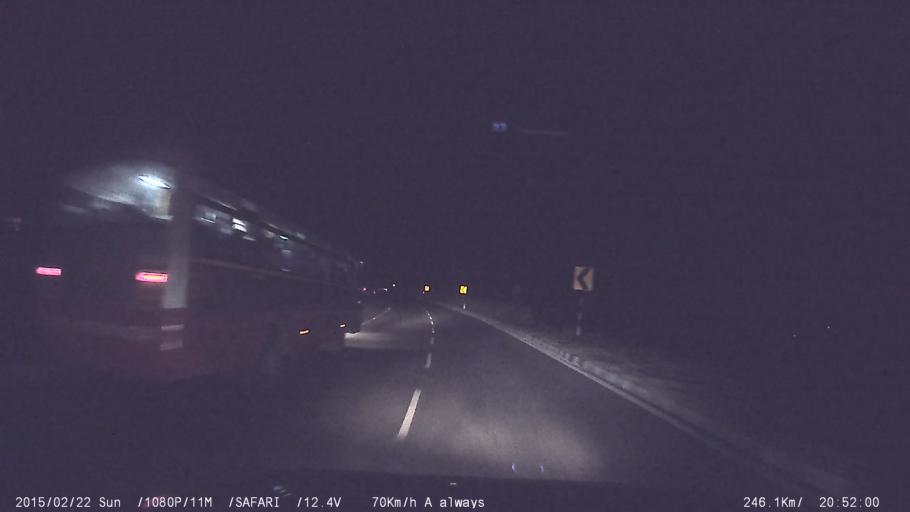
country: IN
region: Tamil Nadu
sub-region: Dindigul
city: Vedasandur
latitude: 10.5478
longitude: 77.9462
